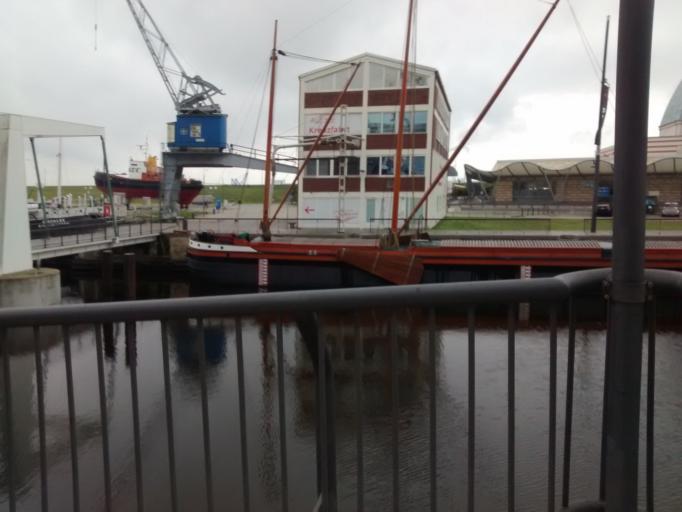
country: DE
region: Bremen
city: Bremerhaven
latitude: 53.5420
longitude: 8.5774
